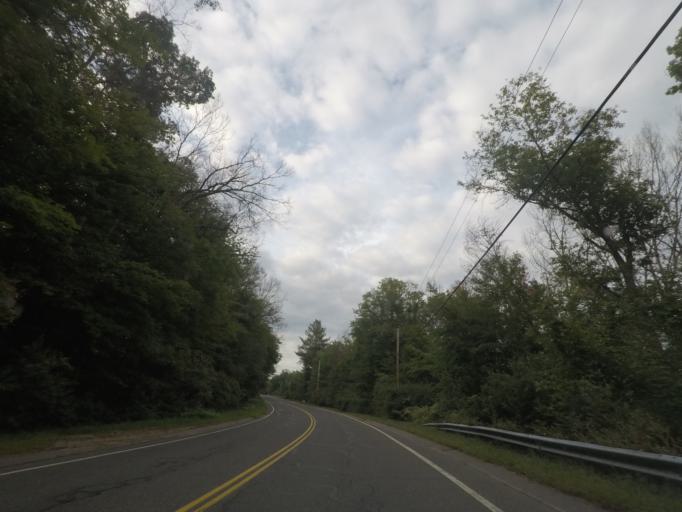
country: US
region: Massachusetts
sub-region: Hampden County
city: Palmer
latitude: 42.1928
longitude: -72.2676
